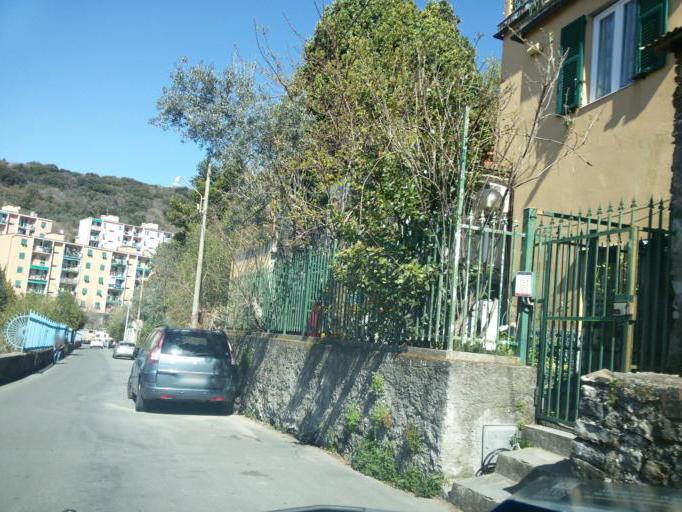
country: IT
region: Liguria
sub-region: Provincia di Genova
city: Genoa
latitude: 44.4141
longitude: 8.9802
